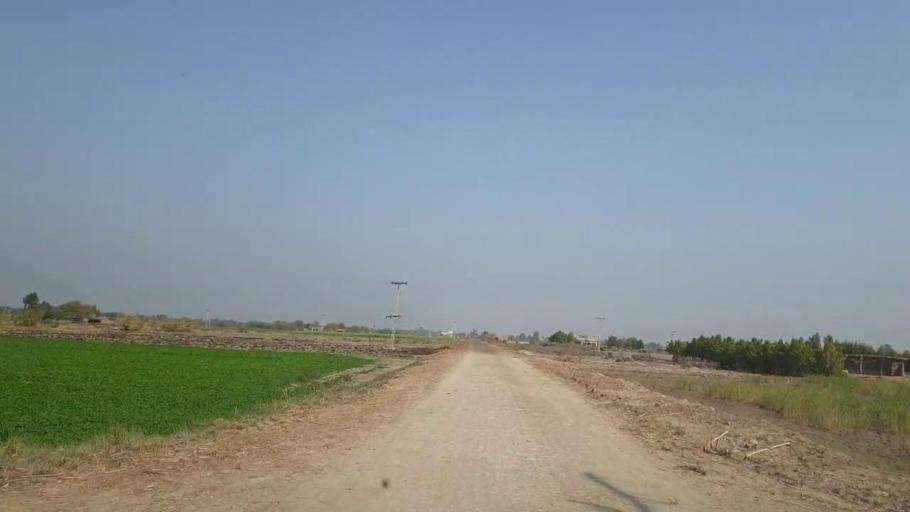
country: PK
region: Sindh
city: Mirpur Khas
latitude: 25.5913
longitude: 69.0148
